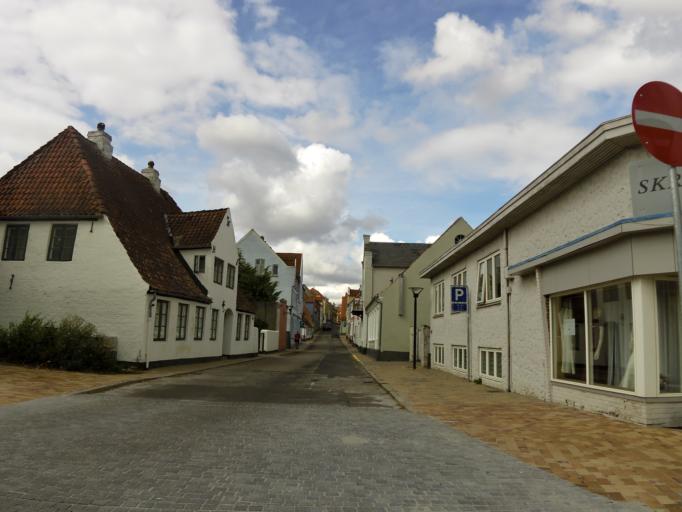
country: DK
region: South Denmark
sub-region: Aabenraa Kommune
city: Aabenraa
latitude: 55.0425
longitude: 9.4158
